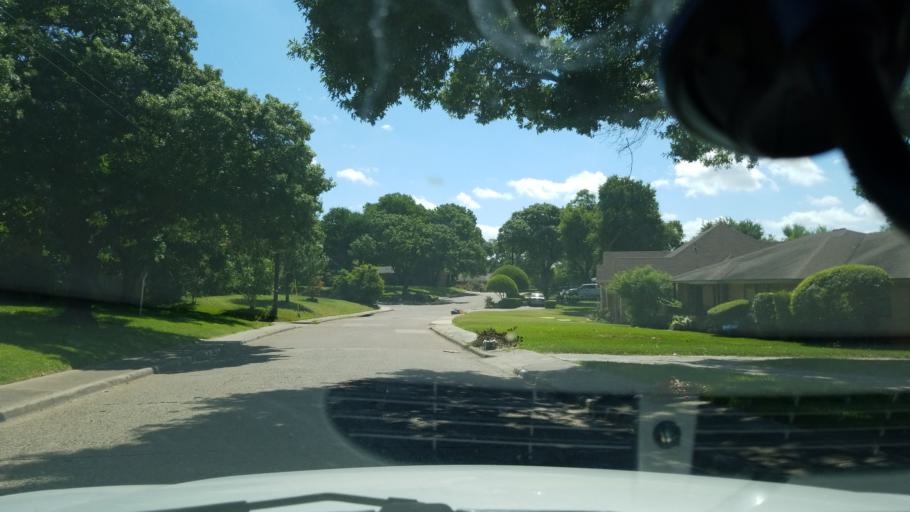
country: US
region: Texas
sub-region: Dallas County
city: Cockrell Hill
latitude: 32.6830
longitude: -96.8322
